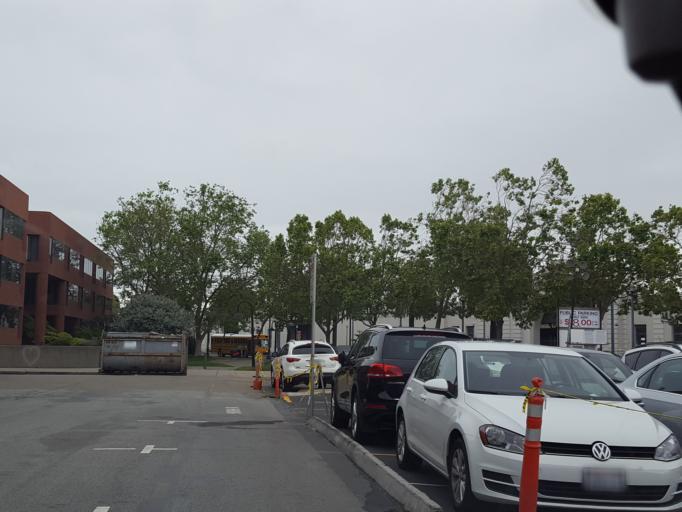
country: US
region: California
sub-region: San Francisco County
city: San Francisco
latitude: 37.8017
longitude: -122.4005
